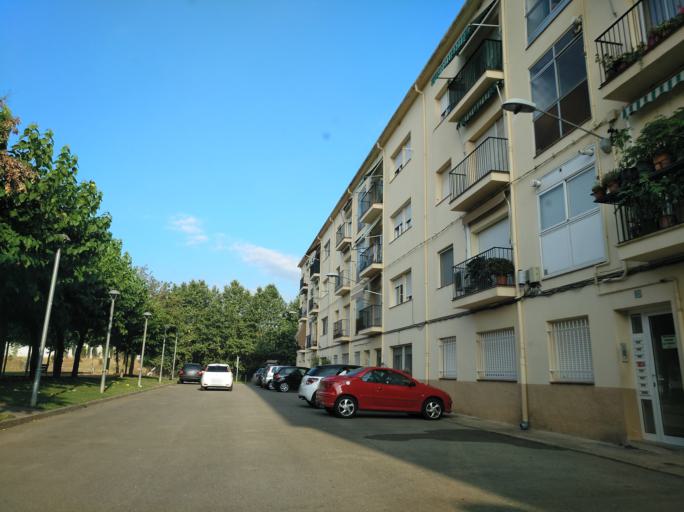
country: ES
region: Catalonia
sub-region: Provincia de Girona
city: Salt
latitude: 41.9743
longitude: 2.7797
